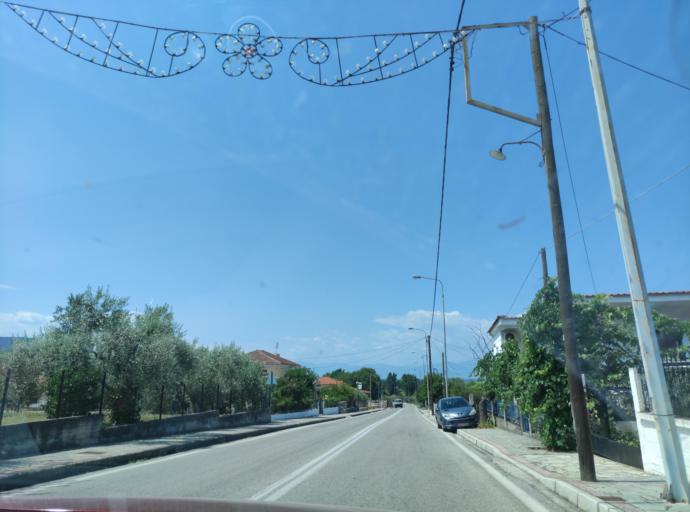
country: GR
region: East Macedonia and Thrace
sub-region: Nomos Kavalas
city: Palaiochori
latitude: 40.9470
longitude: 24.2097
